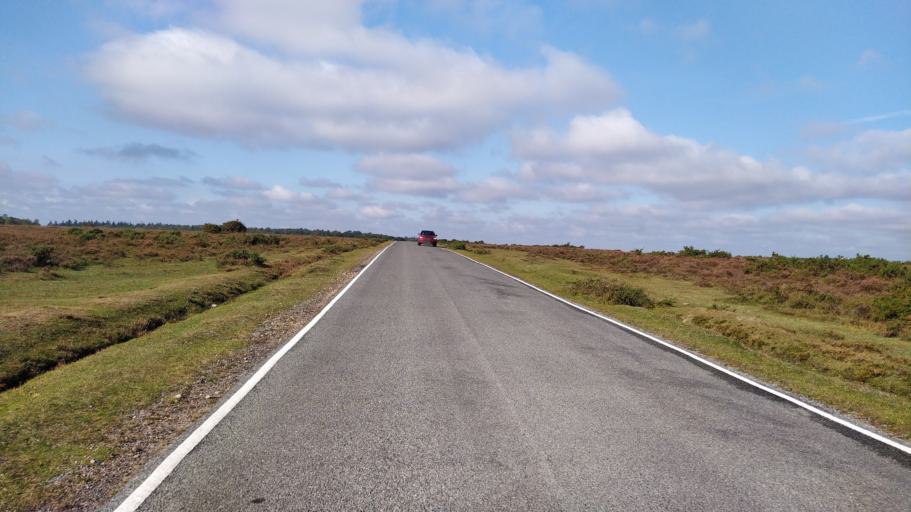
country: GB
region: England
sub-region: Hampshire
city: Sway
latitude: 50.7960
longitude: -1.5974
